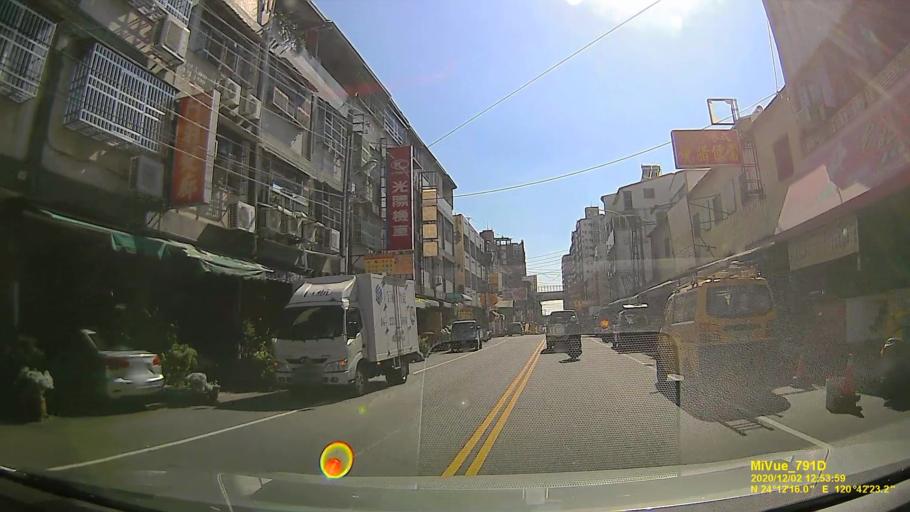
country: TW
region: Taiwan
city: Fengyuan
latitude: 24.2043
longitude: 120.7066
